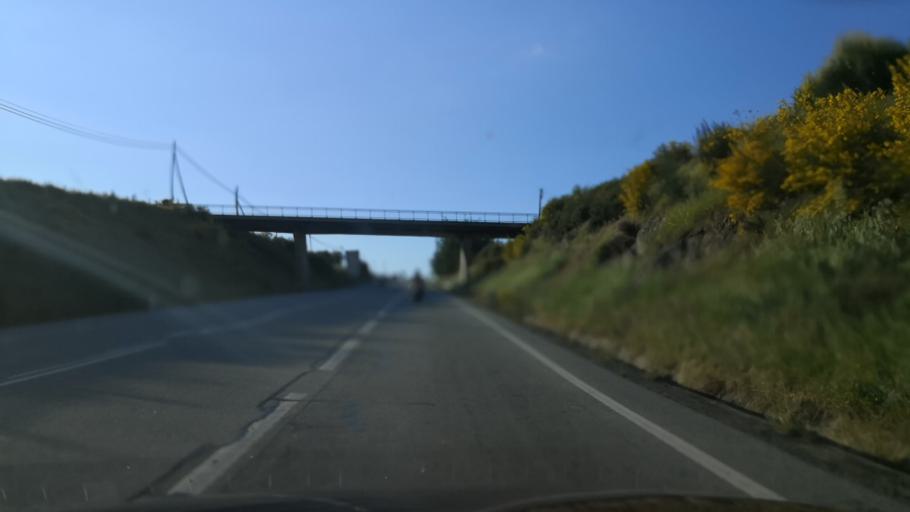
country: PT
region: Portalegre
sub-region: Portalegre
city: Portalegre
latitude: 39.3049
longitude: -7.4408
